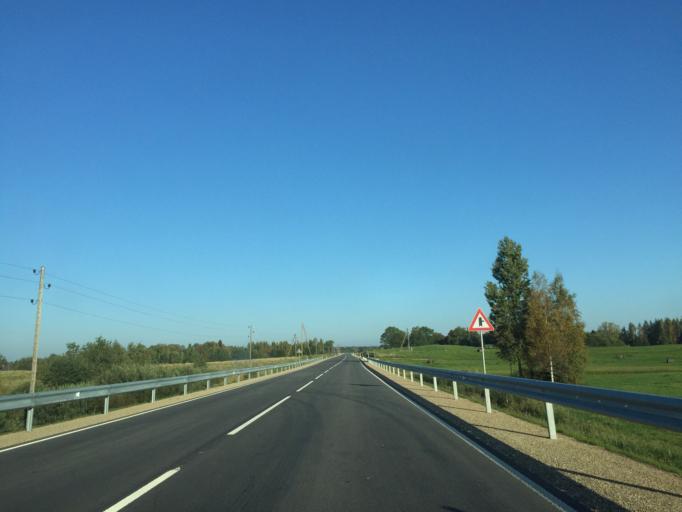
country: LV
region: Vecpiebalga
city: Vecpiebalga
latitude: 57.0874
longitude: 25.7416
